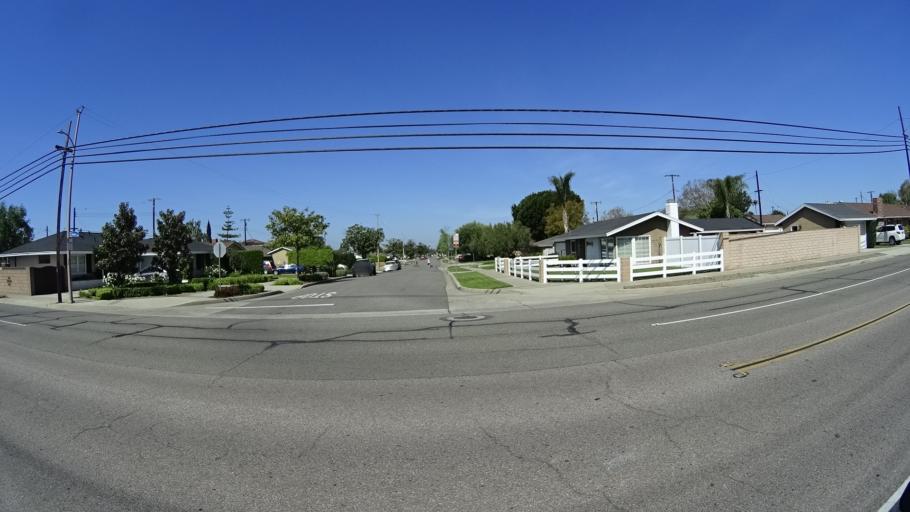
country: US
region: California
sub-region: Orange County
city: Villa Park
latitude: 33.8046
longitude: -117.8219
